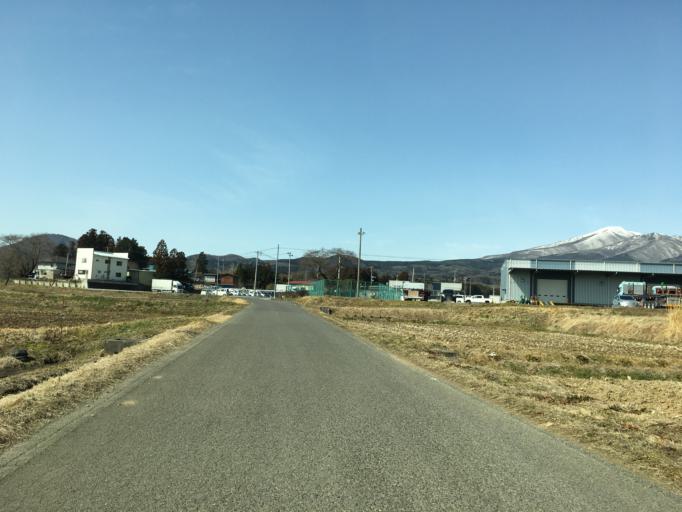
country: JP
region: Fukushima
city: Motomiya
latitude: 37.5474
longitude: 140.3623
